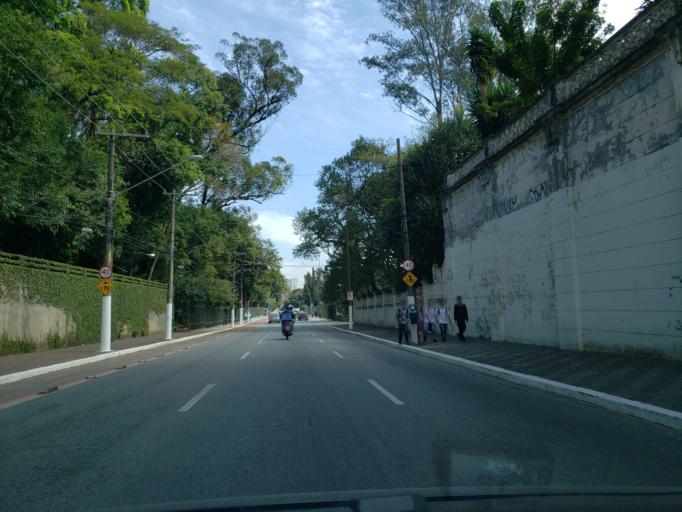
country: BR
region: Sao Paulo
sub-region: Sao Paulo
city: Sao Paulo
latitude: -23.5835
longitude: -46.6084
